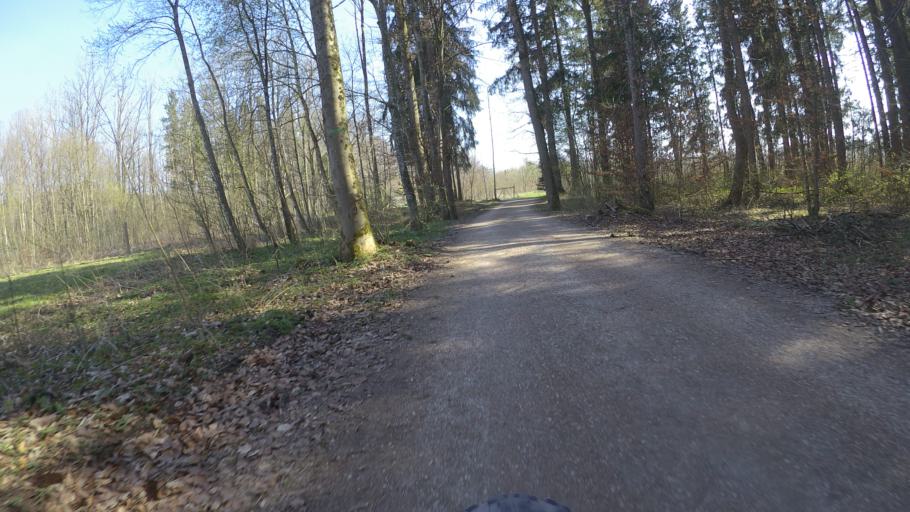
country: DE
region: Bavaria
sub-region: Upper Bavaria
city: Traunreut
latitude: 47.9553
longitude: 12.5821
